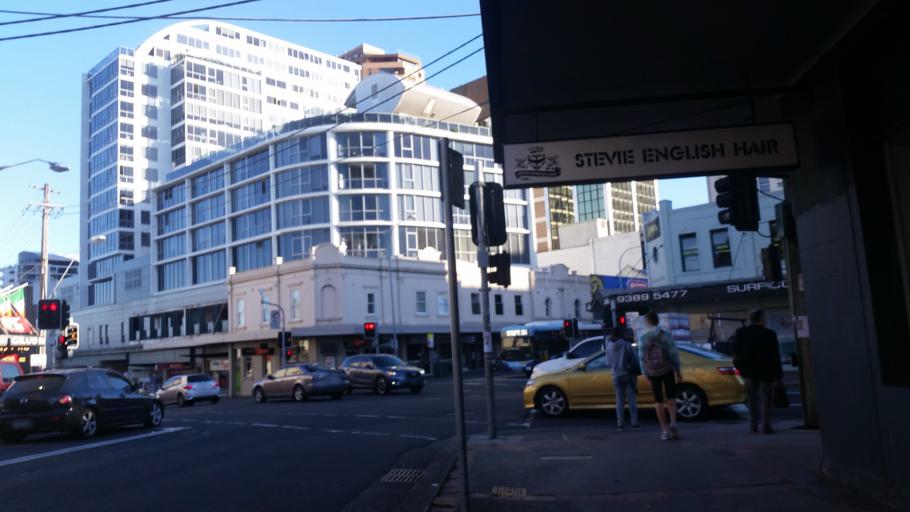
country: AU
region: New South Wales
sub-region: Waverley
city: Bondi Junction
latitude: -33.8940
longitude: 151.2496
